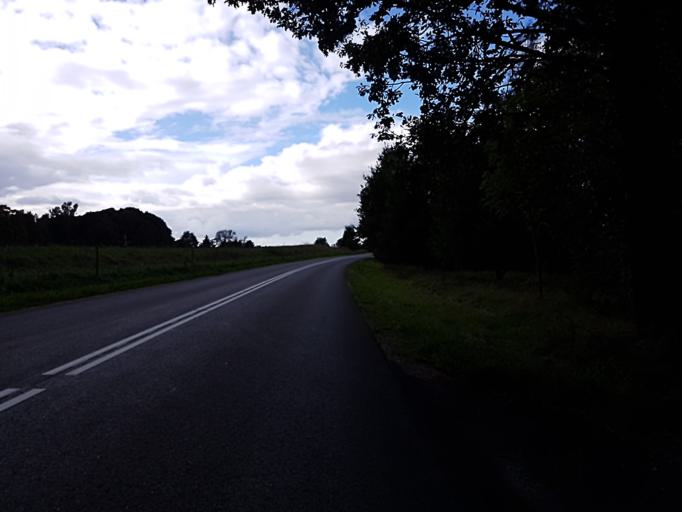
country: DK
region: Capital Region
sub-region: Egedal Kommune
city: Stenlose
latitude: 55.7398
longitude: 12.1904
